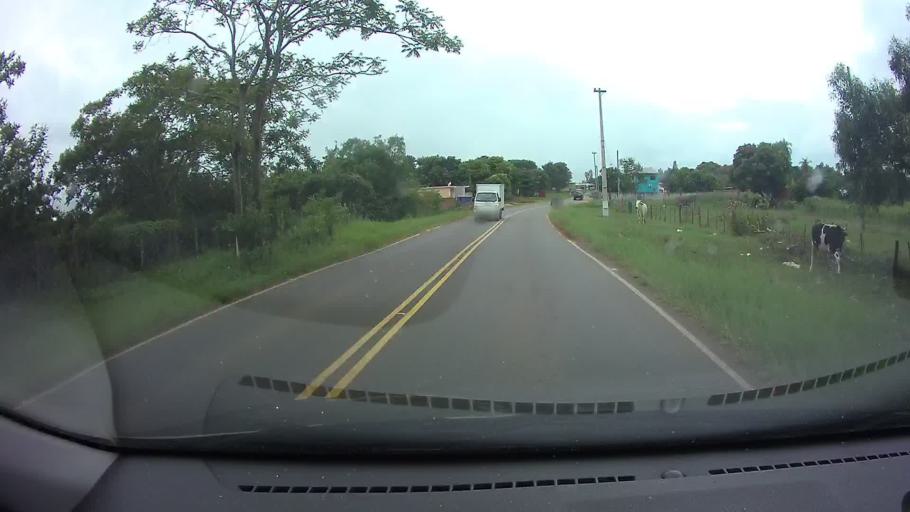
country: PY
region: Paraguari
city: Carapegua
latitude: -25.7555
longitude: -57.2575
